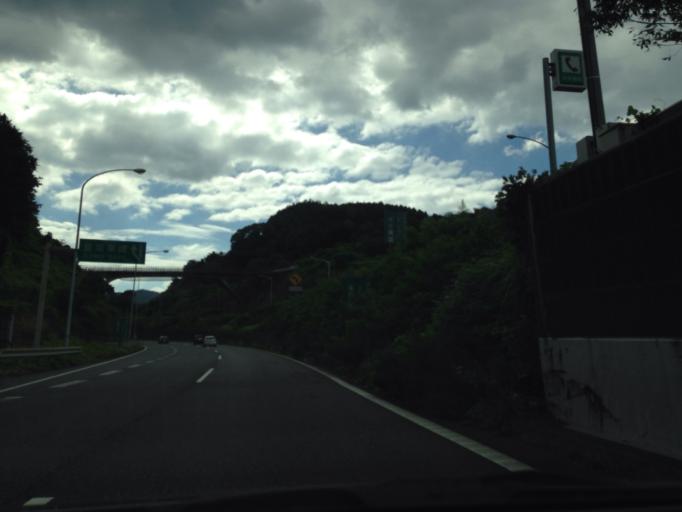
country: JP
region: Kanagawa
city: Odawara
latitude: 35.3663
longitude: 139.0914
